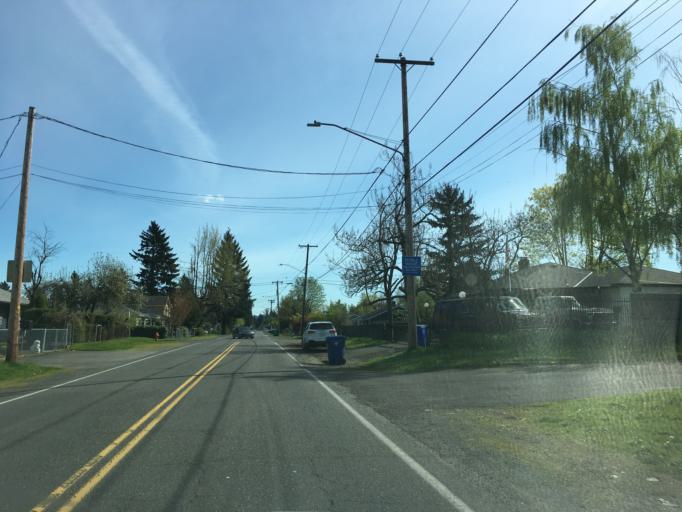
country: US
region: Oregon
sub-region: Multnomah County
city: Lents
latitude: 45.5414
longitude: -122.5490
